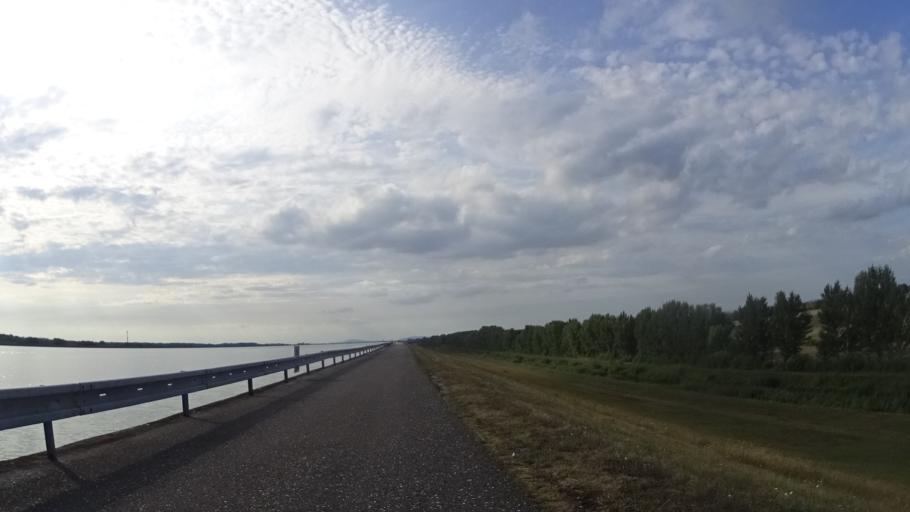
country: HU
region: Gyor-Moson-Sopron
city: Halaszi
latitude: 47.9581
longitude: 17.4276
